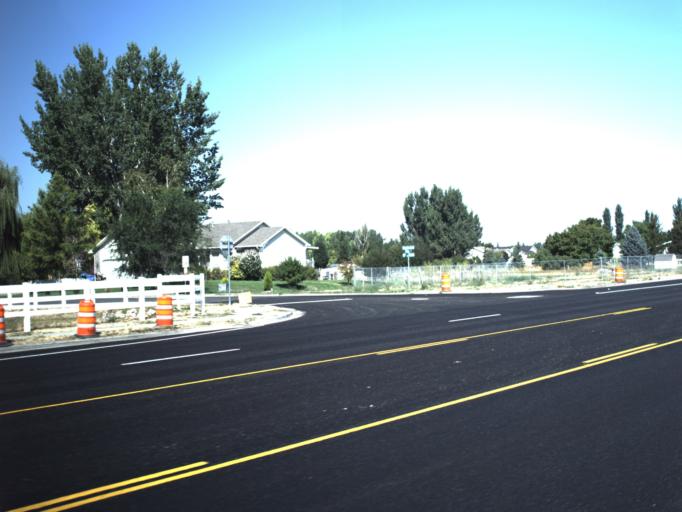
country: US
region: Utah
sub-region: Cache County
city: Nibley
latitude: 41.6638
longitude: -111.8336
